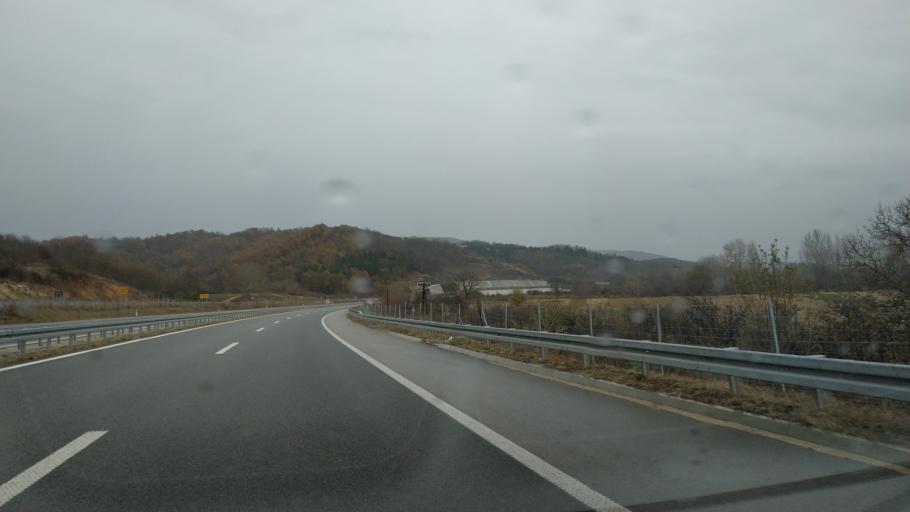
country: RS
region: Central Serbia
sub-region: Pirotski Okrug
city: Bela Palanka
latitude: 43.2323
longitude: 22.4481
